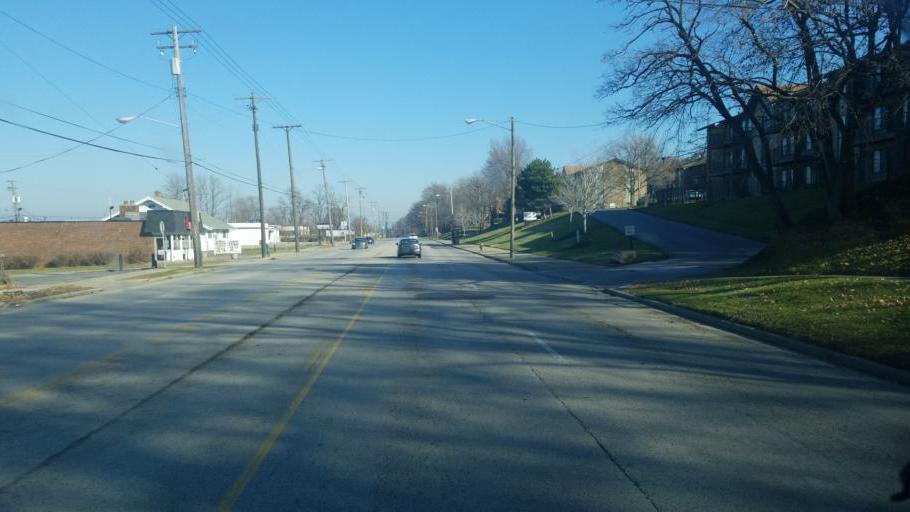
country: US
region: Ohio
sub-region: Cuyahoga County
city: Richmond Heights
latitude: 41.5611
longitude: -81.5444
